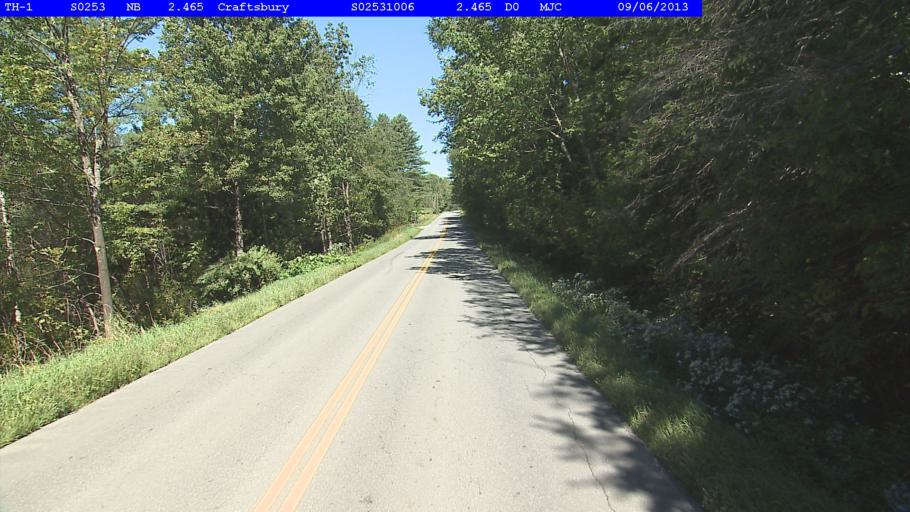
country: US
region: Vermont
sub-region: Caledonia County
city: Hardwick
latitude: 44.6439
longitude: -72.3792
